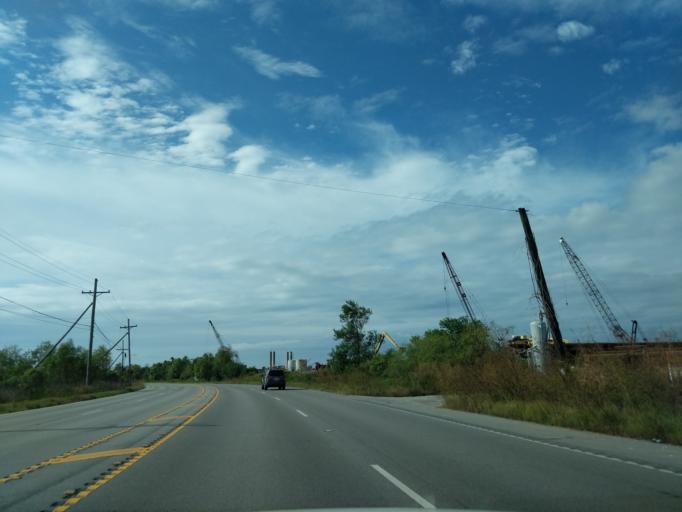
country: US
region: Louisiana
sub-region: Saint Tammany Parish
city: Eden Isle
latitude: 30.0755
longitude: -89.8427
